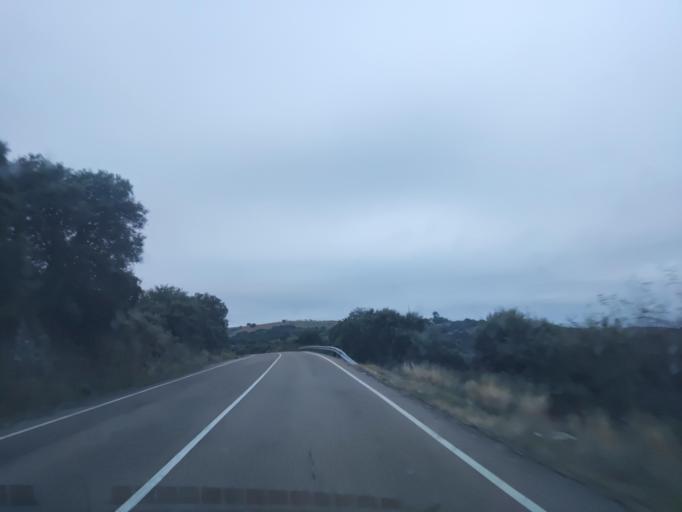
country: ES
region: Castille and Leon
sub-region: Provincia de Salamanca
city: Hinojosa de Duero
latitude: 40.9747
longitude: -6.8374
